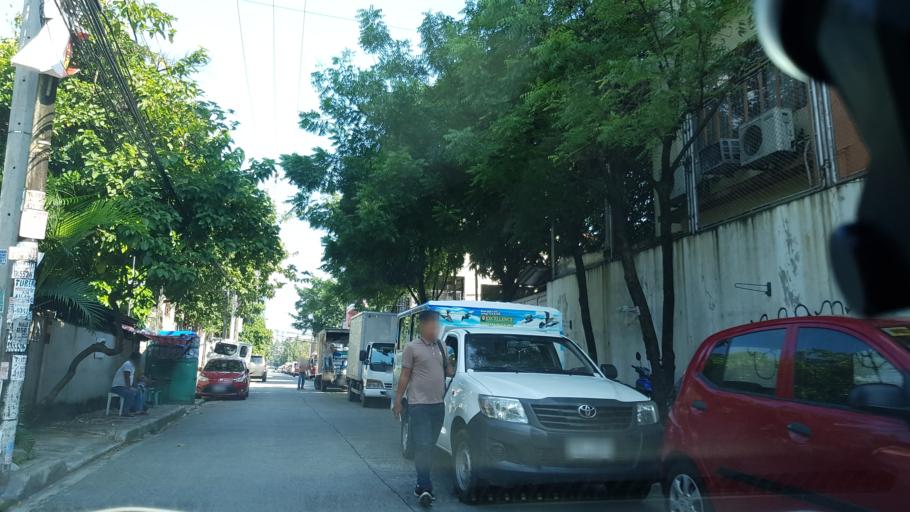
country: PH
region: Metro Manila
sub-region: Quezon City
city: Quezon City
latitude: 14.6241
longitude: 121.0448
